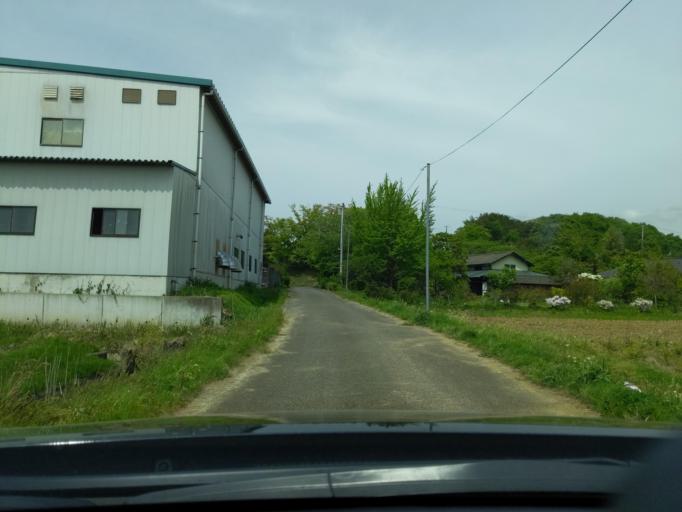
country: JP
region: Fukushima
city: Koriyama
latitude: 37.4061
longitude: 140.2741
